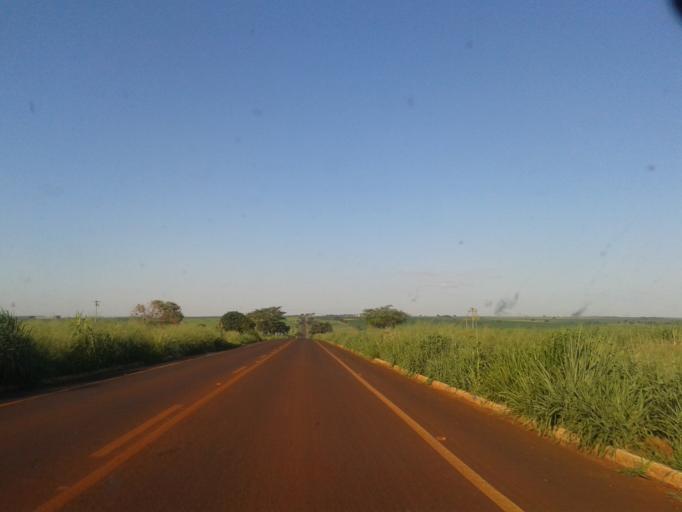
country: BR
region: Minas Gerais
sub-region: Capinopolis
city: Capinopolis
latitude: -18.7042
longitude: -49.6792
